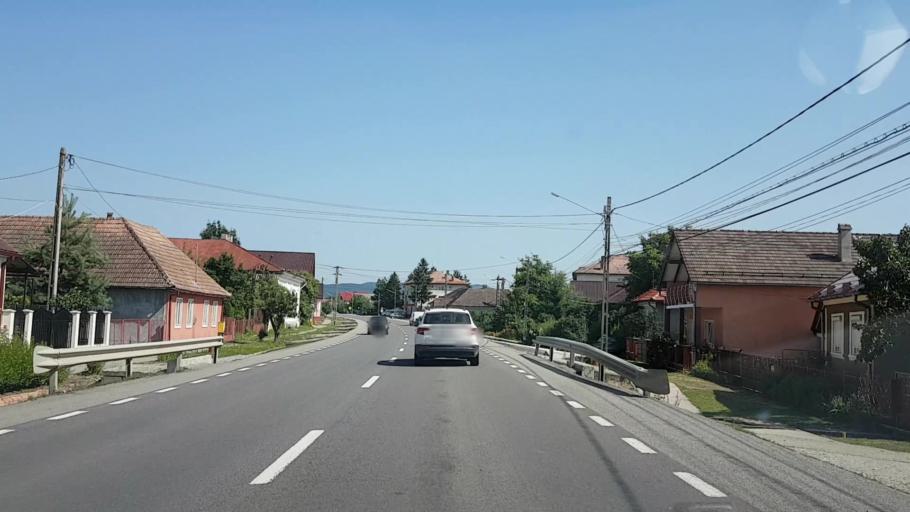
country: RO
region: Bistrita-Nasaud
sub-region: Comuna Sieu-Magherus
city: Sieu-Magherus
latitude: 47.0924
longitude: 24.3713
